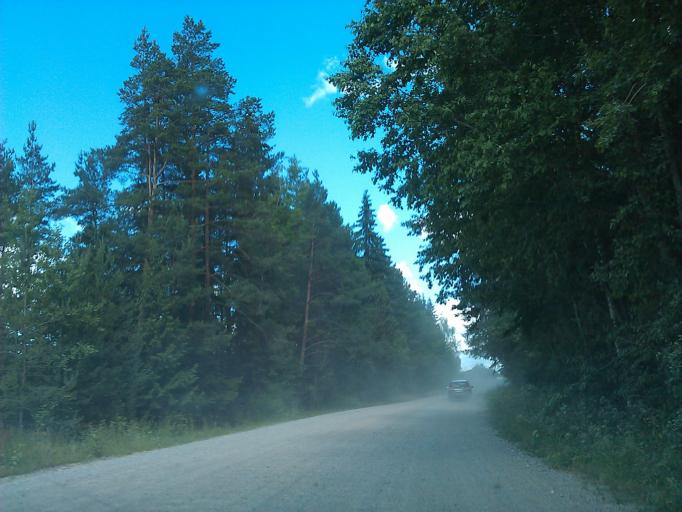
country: LV
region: Vilanu
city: Vilani
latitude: 56.5846
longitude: 26.9443
